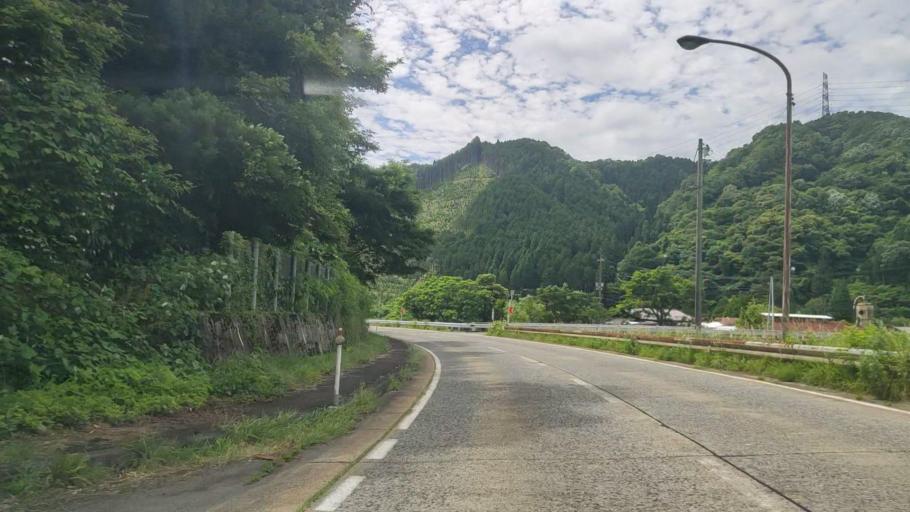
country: JP
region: Okayama
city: Niimi
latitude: 35.1637
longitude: 133.5793
